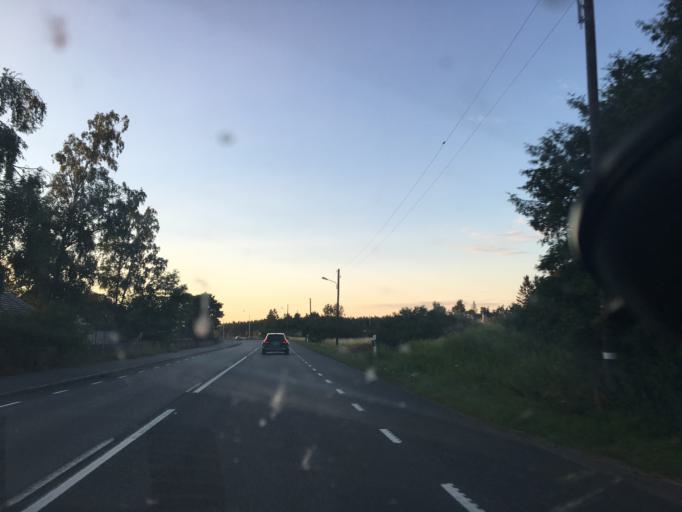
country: SE
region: Skane
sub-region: Kristianstads Kommun
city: Ahus
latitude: 55.9628
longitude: 14.2812
